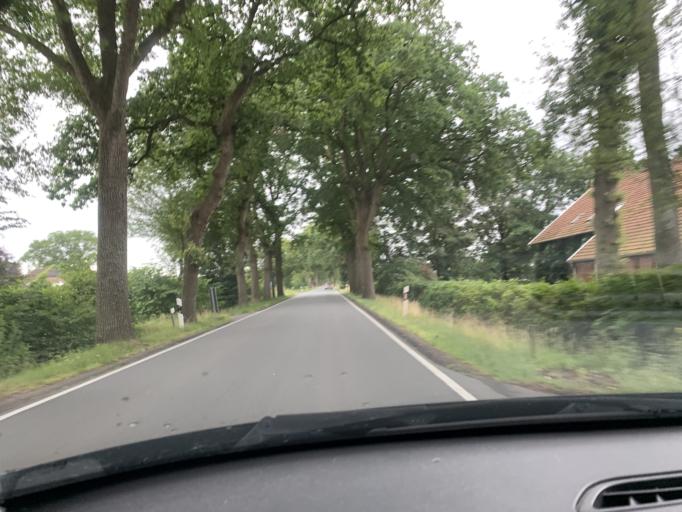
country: DE
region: Lower Saxony
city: Westerstede
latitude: 53.2570
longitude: 7.9551
